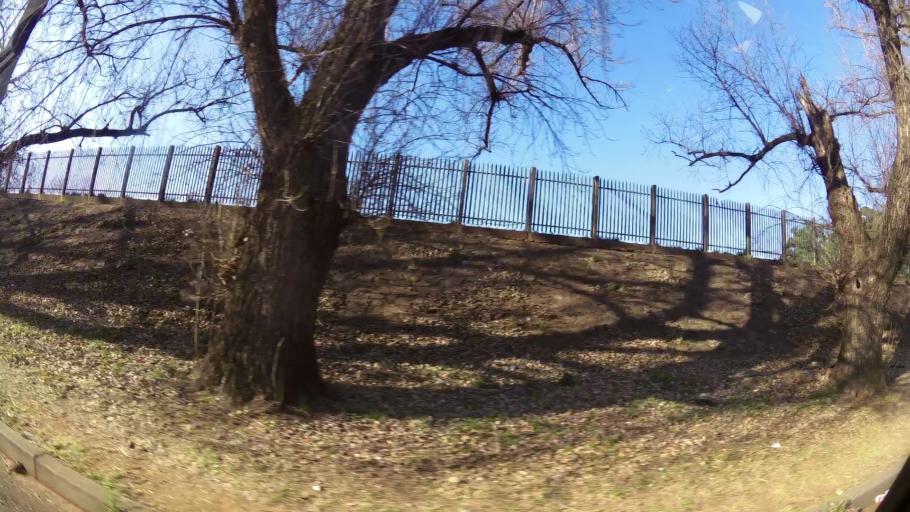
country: ZA
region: Gauteng
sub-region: City of Johannesburg Metropolitan Municipality
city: Johannesburg
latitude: -26.1895
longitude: 28.0983
